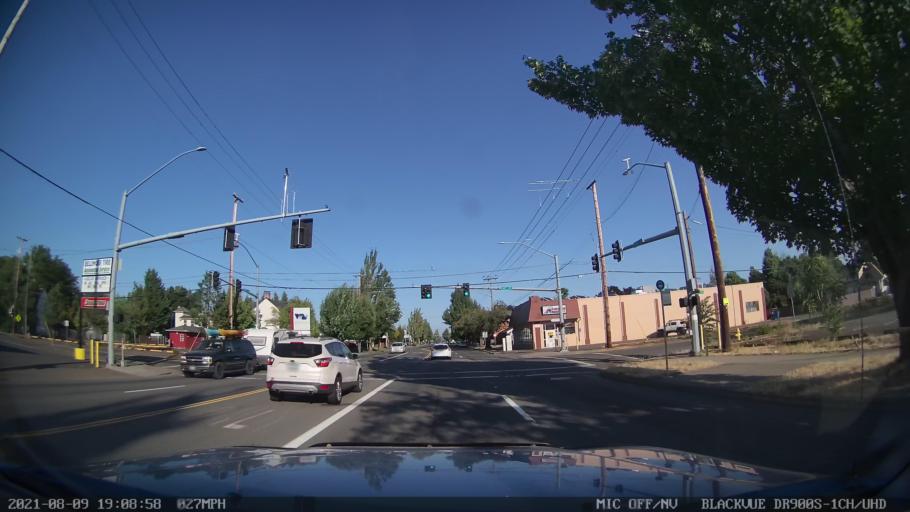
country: US
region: Oregon
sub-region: Marion County
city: Salem
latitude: 44.9363
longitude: -123.0248
